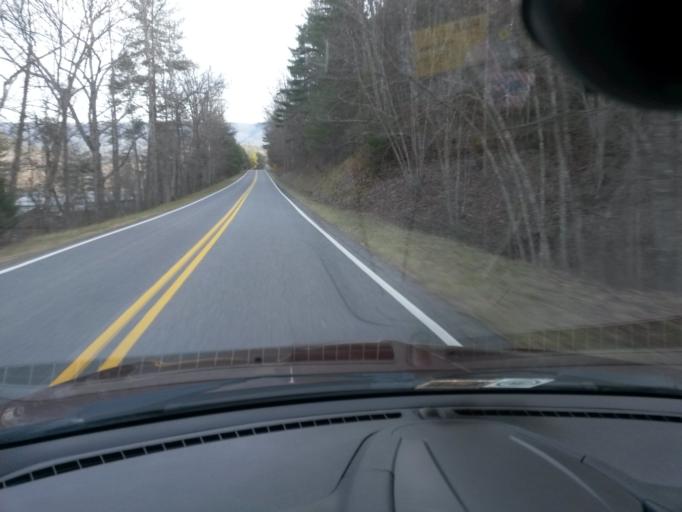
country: US
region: Virginia
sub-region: Alleghany County
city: Clifton Forge
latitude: 37.8730
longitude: -79.7433
